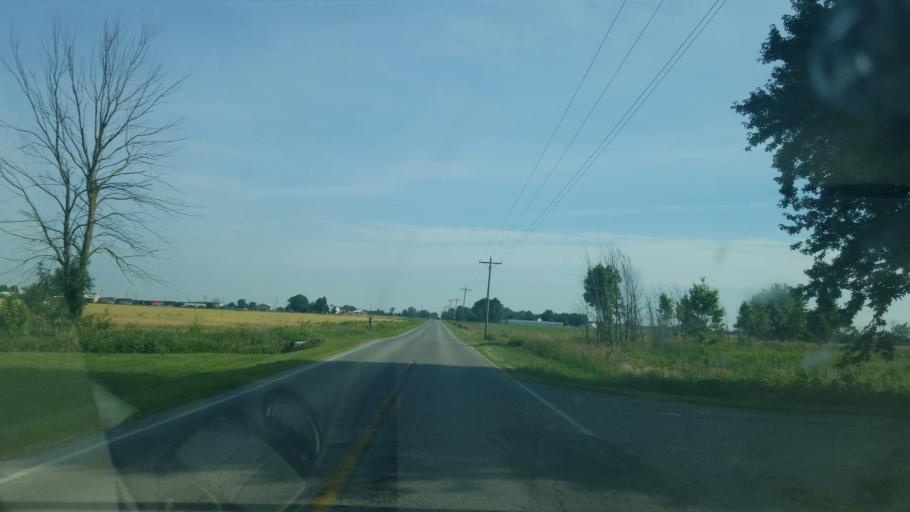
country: US
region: Ohio
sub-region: Hancock County
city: Findlay
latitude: 40.9970
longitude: -83.6985
